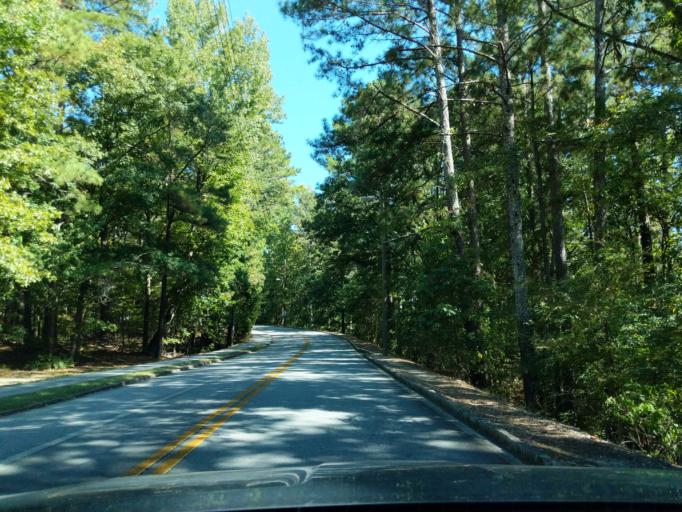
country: US
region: Georgia
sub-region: DeKalb County
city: Stone Mountain
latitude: 33.7986
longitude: -84.1410
